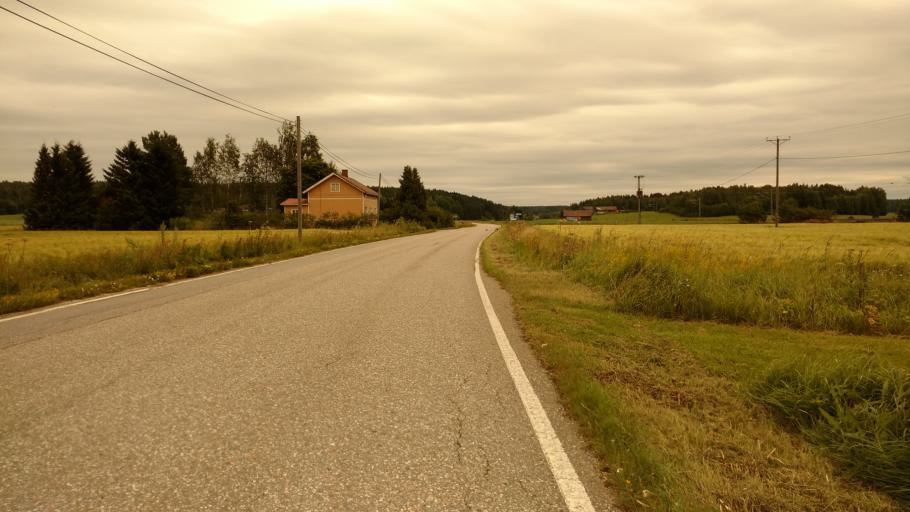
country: FI
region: Varsinais-Suomi
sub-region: Loimaa
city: Marttila
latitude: 60.4169
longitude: 22.8568
